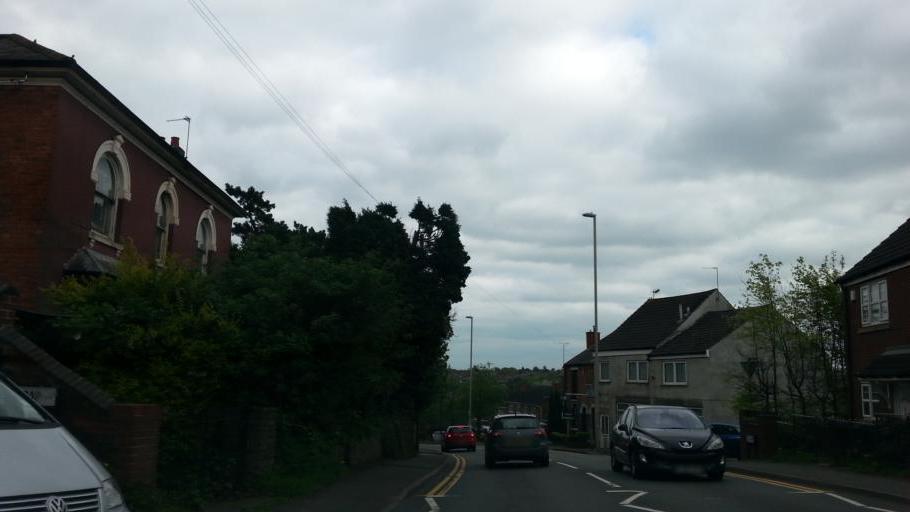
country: GB
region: England
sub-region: Sandwell
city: Cradley Heath
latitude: 52.4577
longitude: -2.0823
